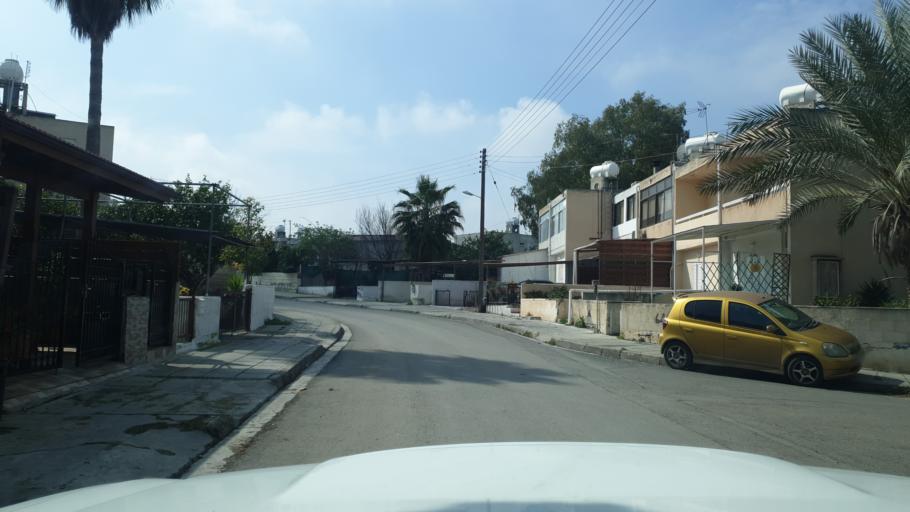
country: CY
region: Lefkosia
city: Kato Deftera
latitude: 35.0877
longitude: 33.2740
